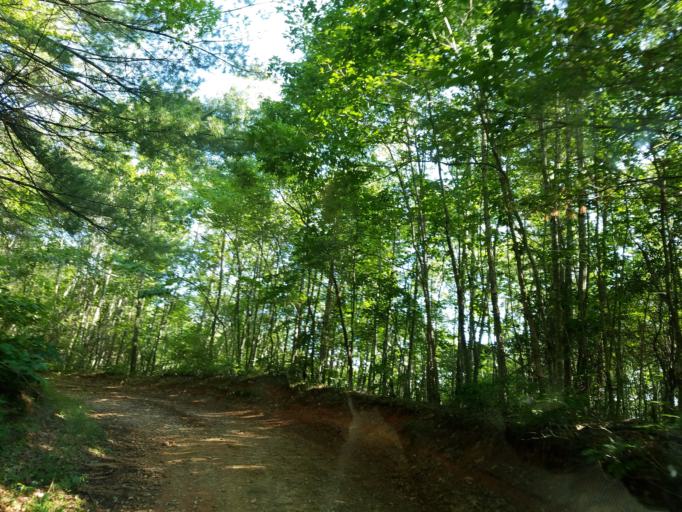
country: US
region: Georgia
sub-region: Fannin County
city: Blue Ridge
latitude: 34.7925
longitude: -84.2120
